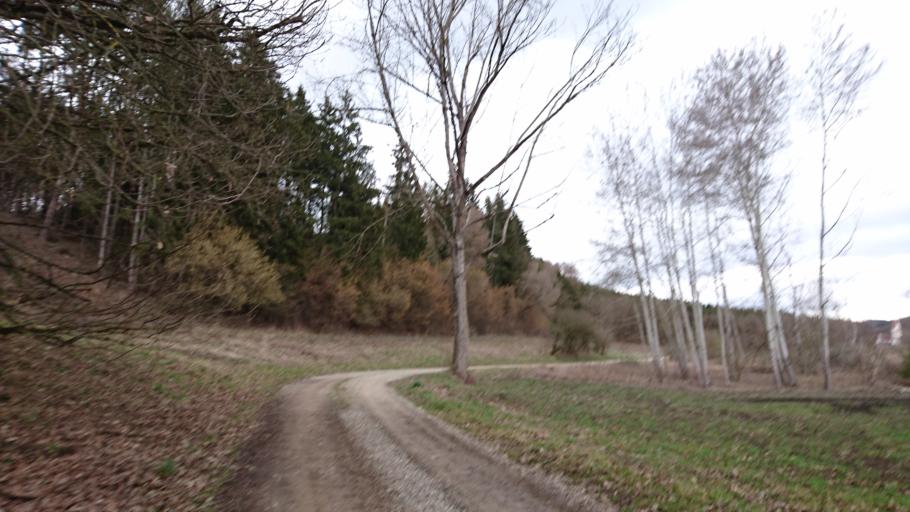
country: DE
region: Bavaria
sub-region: Swabia
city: Altenmunster
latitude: 48.4318
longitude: 10.5853
